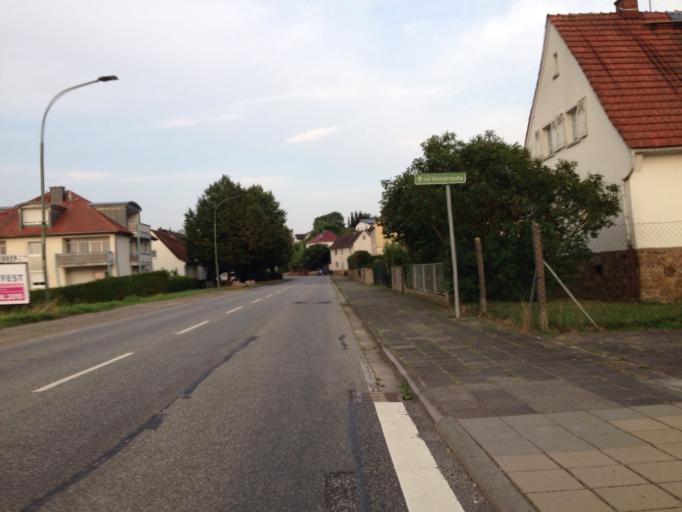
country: DE
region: Hesse
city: Allendorf an der Lahn
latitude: 50.5591
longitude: 8.6382
